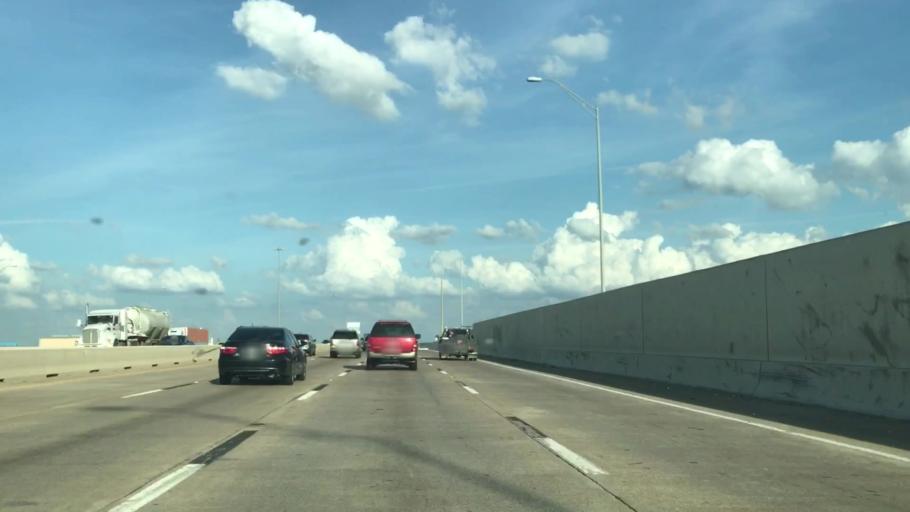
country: US
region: Texas
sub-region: Dallas County
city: Grand Prairie
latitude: 32.7619
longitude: -96.9592
